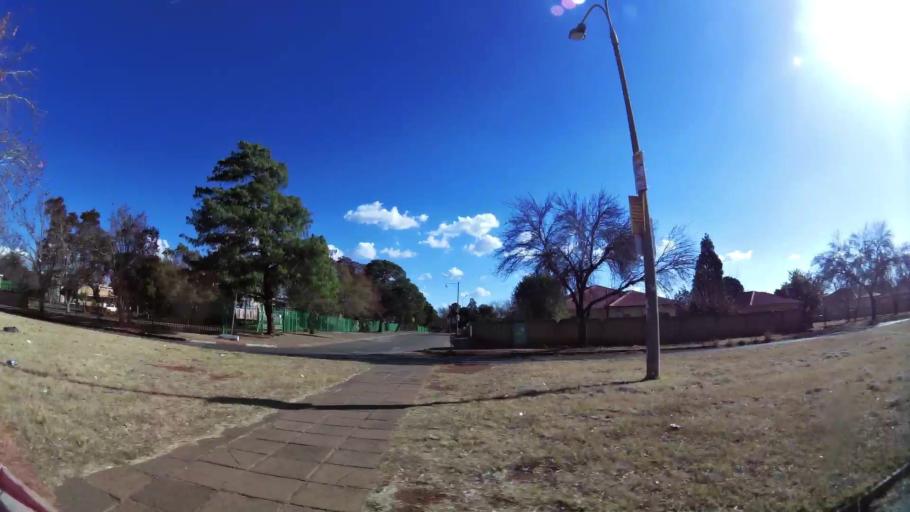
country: ZA
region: Gauteng
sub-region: West Rand District Municipality
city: Carletonville
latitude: -26.3597
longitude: 27.3920
